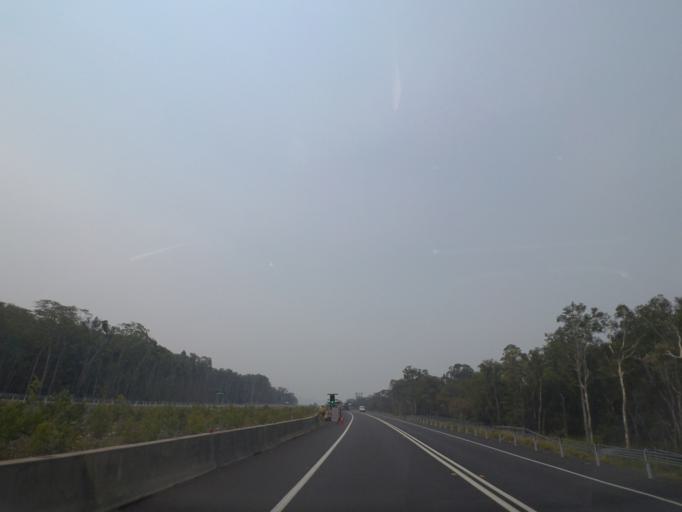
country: AU
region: New South Wales
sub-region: Ballina
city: Ballina
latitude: -28.9131
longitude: 153.4785
